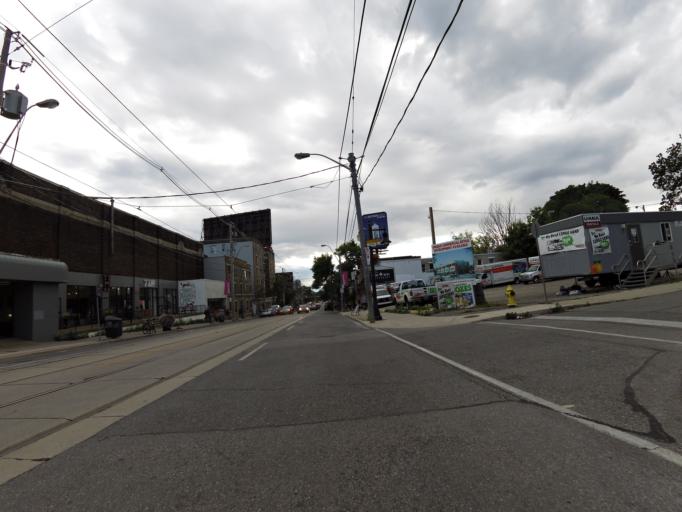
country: CA
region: Ontario
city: Toronto
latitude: 43.6392
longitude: -79.4438
